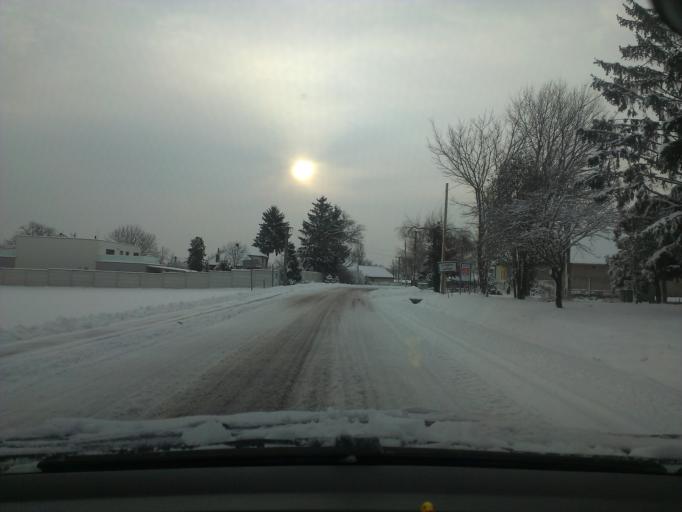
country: SK
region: Trnavsky
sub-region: Okres Trnava
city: Piestany
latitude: 48.5276
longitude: 17.9629
